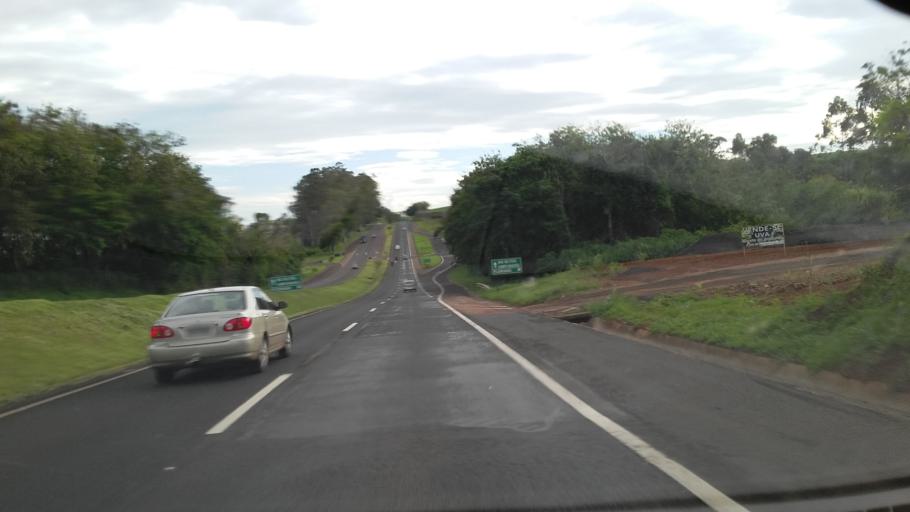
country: BR
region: Parana
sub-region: Paicandu
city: Paicandu
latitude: -23.5190
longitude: -52.0286
